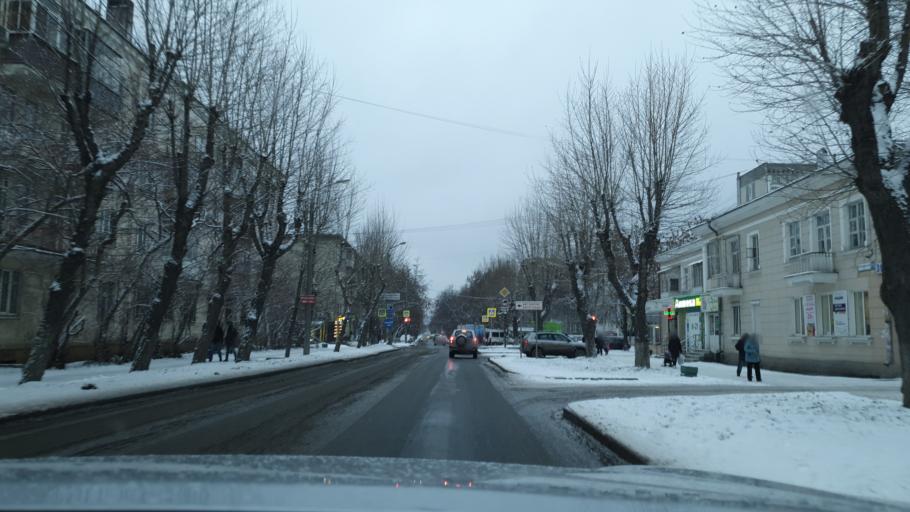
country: RU
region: Sverdlovsk
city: Istok
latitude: 56.7537
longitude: 60.7085
